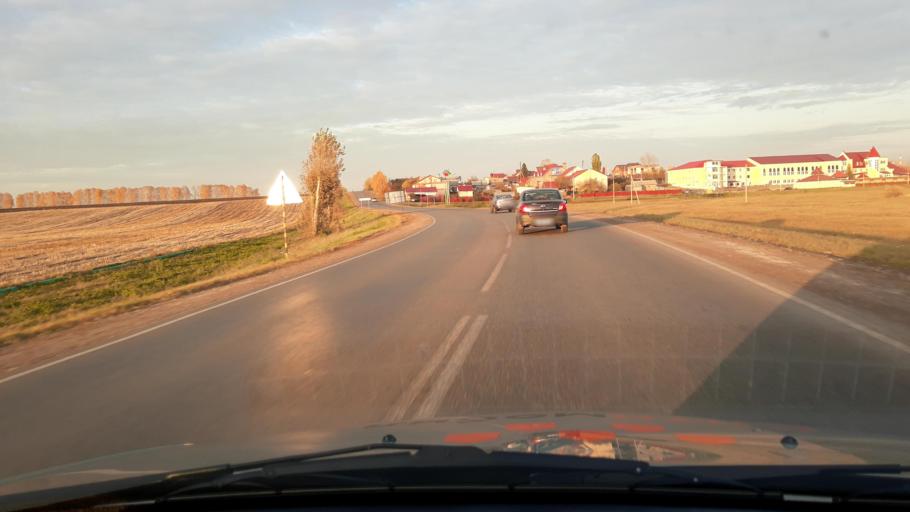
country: RU
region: Bashkortostan
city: Ufa
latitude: 54.8176
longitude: 55.9829
